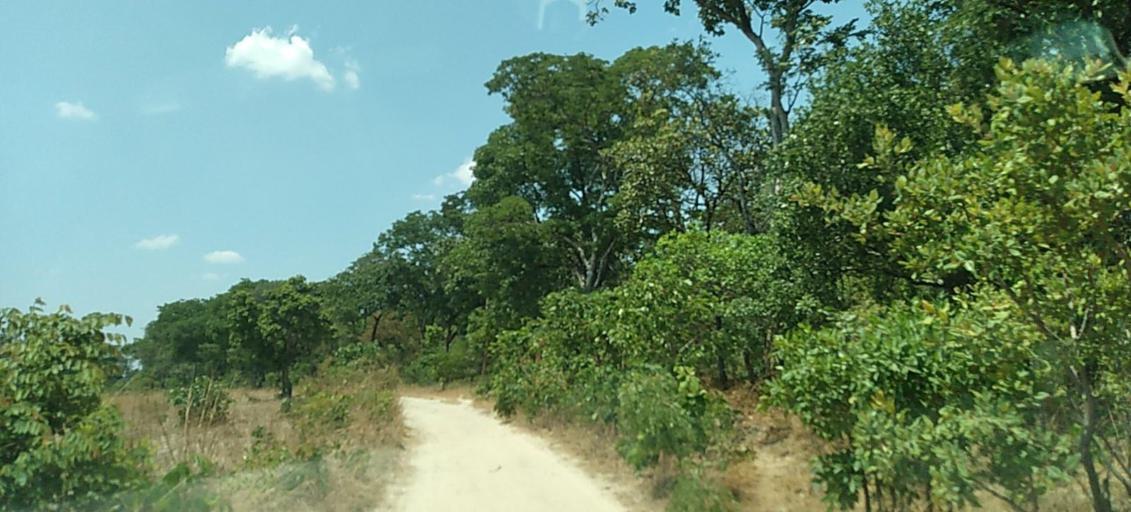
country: ZM
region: Central
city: Kapiri Mposhi
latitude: -13.6622
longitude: 28.4913
